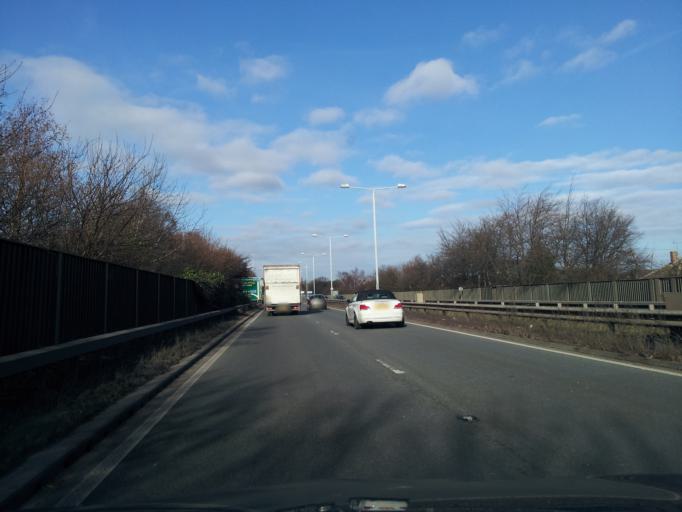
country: GB
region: England
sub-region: Nottinghamshire
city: Ruddington
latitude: 52.9179
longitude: -1.1619
